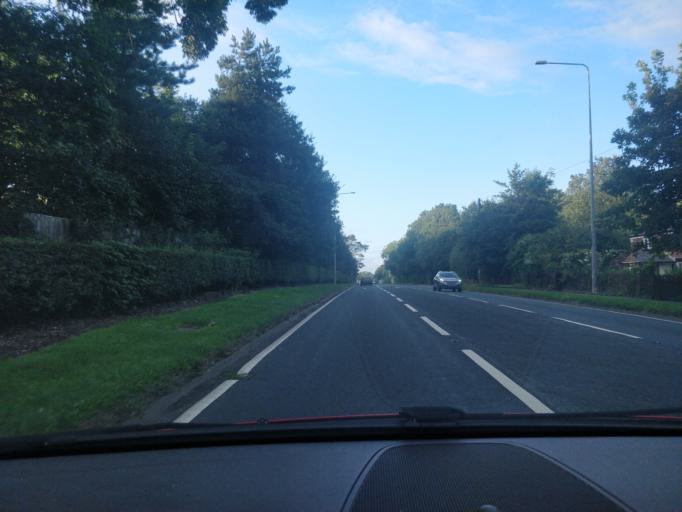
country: GB
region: England
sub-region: Lancashire
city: Tarleton
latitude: 53.6804
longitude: -2.8170
